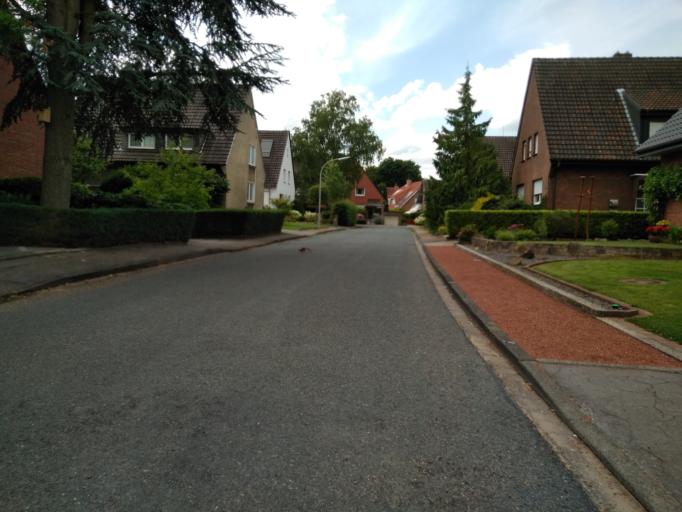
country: DE
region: North Rhine-Westphalia
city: Dorsten
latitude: 51.6649
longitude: 6.9451
